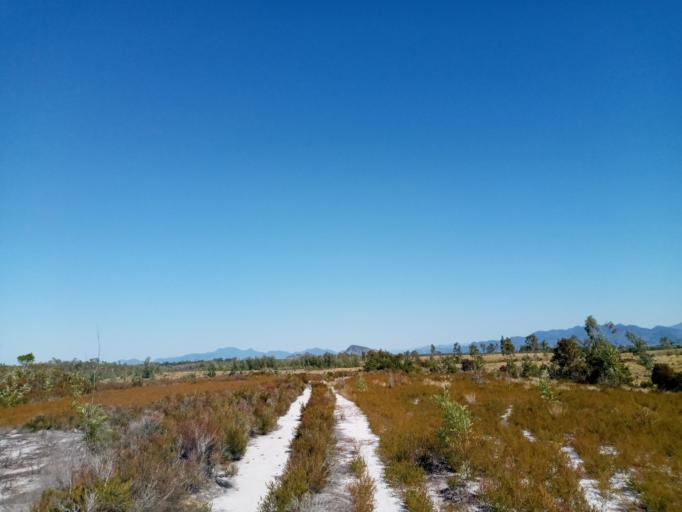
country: MG
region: Atsimo-Atsinanana
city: Vohipaho
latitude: -24.2475
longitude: 47.3183
